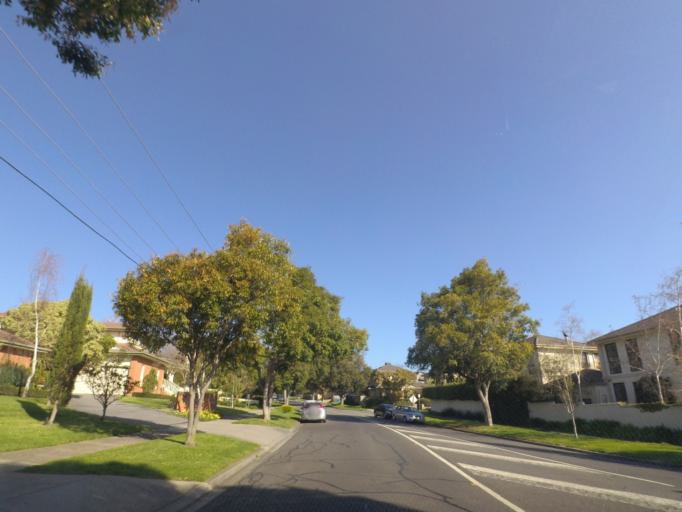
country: AU
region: Victoria
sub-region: Whitehorse
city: Mont Albert North
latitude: -37.7982
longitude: 145.1034
